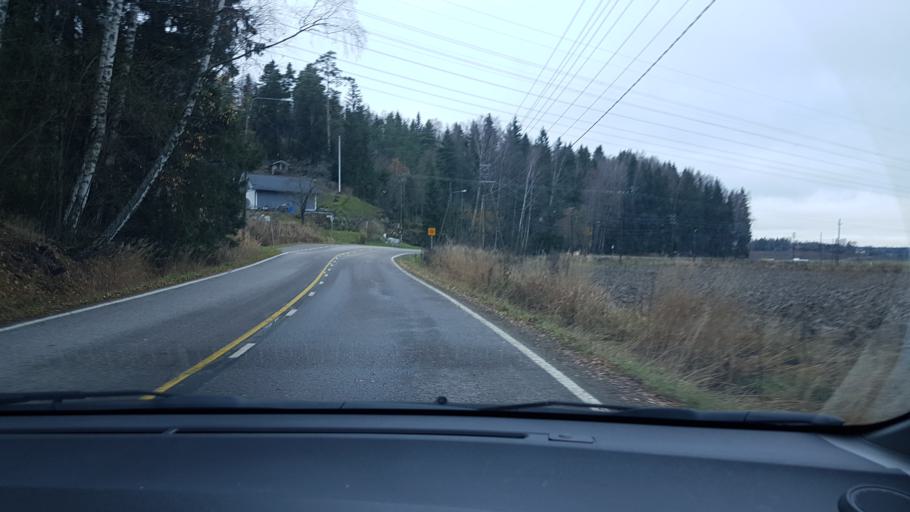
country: FI
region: Uusimaa
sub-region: Helsinki
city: Vantaa
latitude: 60.2717
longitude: 25.1395
